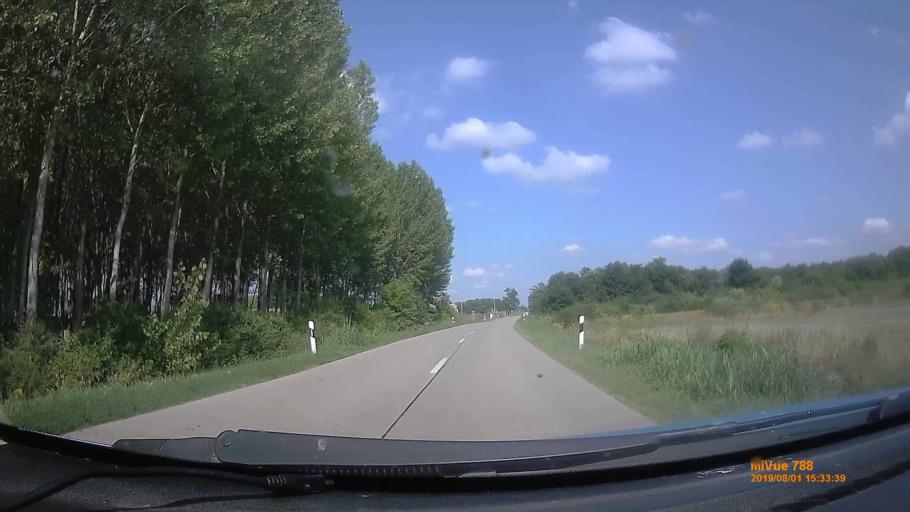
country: HU
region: Baranya
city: Sellye
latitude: 45.9556
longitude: 17.8838
